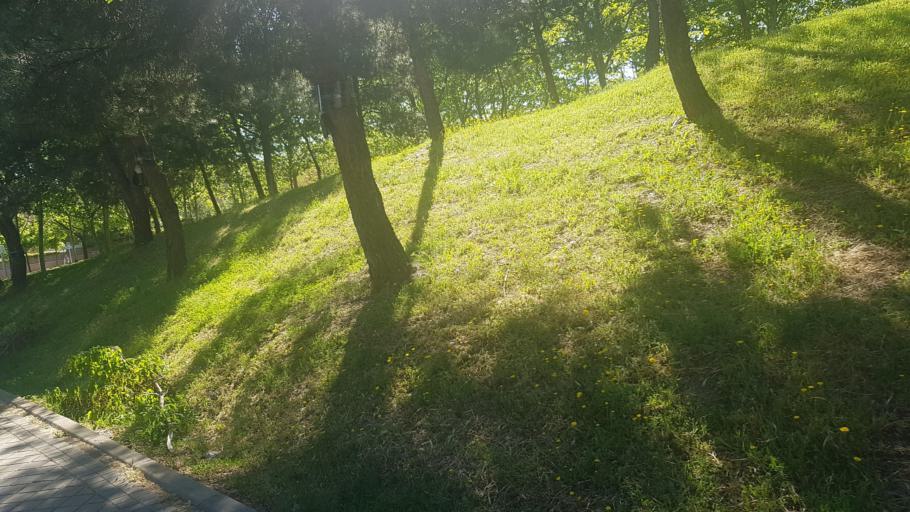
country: ES
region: Madrid
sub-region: Provincia de Madrid
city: Pozuelo de Alarcon
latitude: 40.4676
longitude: -3.7872
